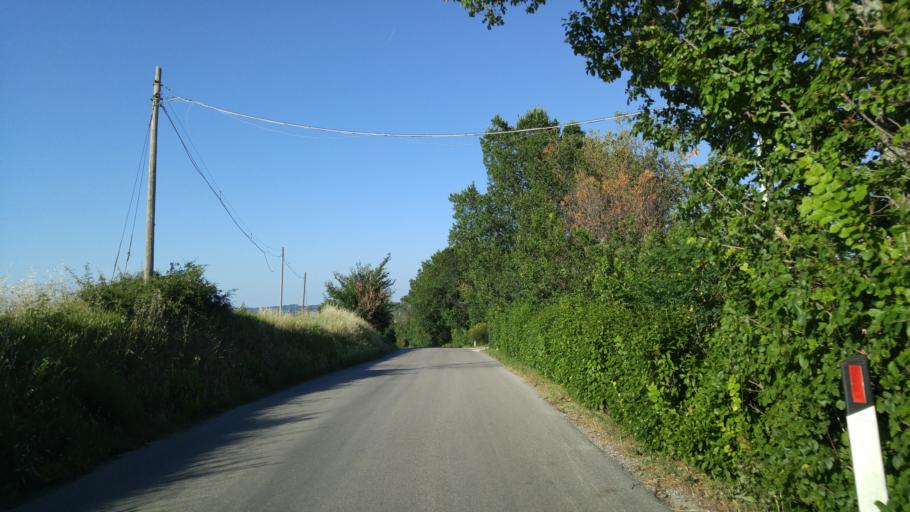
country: IT
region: The Marches
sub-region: Provincia di Pesaro e Urbino
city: Mombaroccio
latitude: 43.7955
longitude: 12.8773
